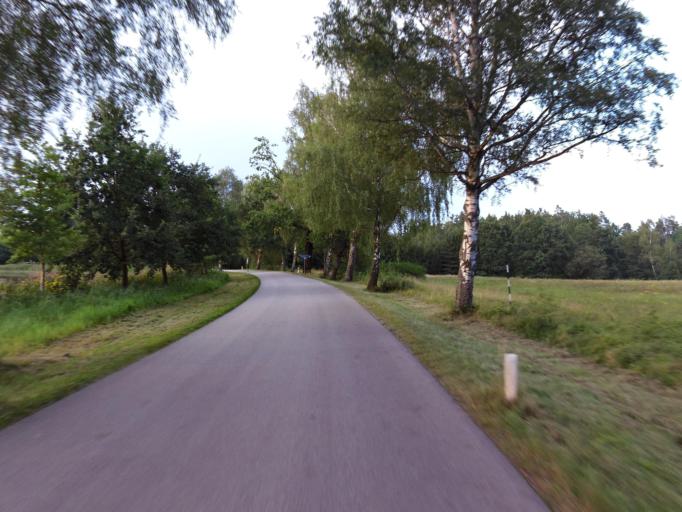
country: CZ
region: Jihocesky
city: Chlum u Trebone
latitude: 48.9774
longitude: 14.9441
